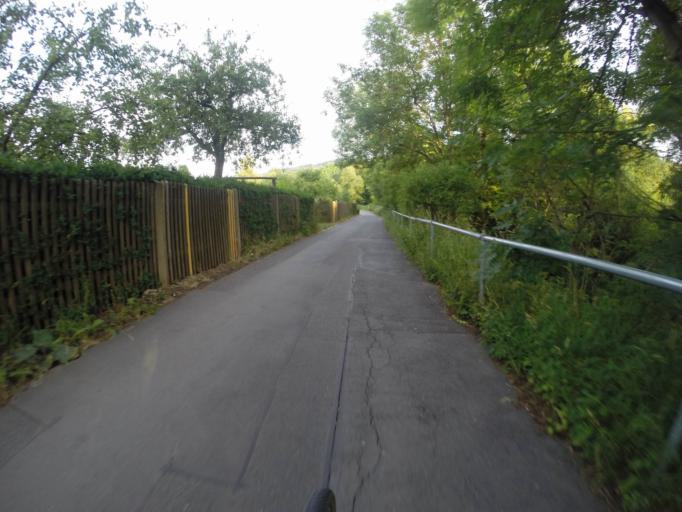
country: DE
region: Thuringia
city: Jena
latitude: 50.9351
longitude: 11.6115
